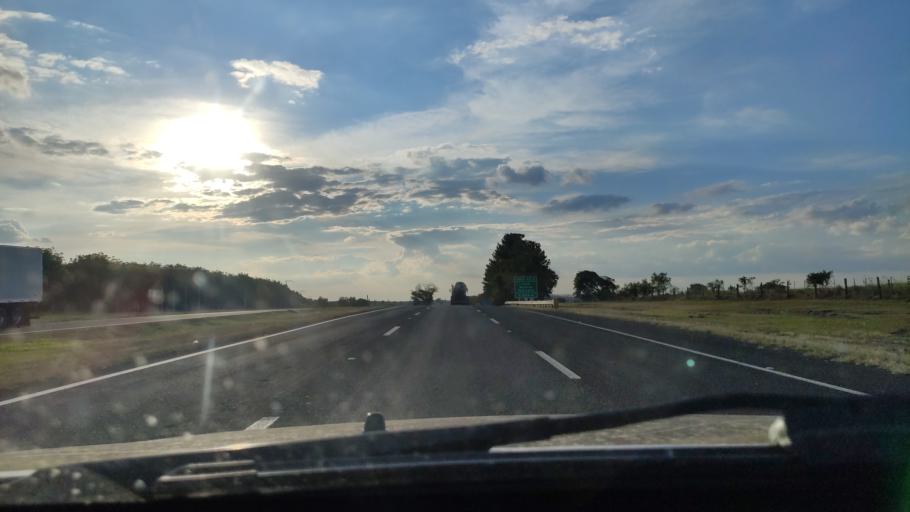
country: BR
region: Sao Paulo
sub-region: Rancharia
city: Rancharia
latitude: -22.4452
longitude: -50.9911
